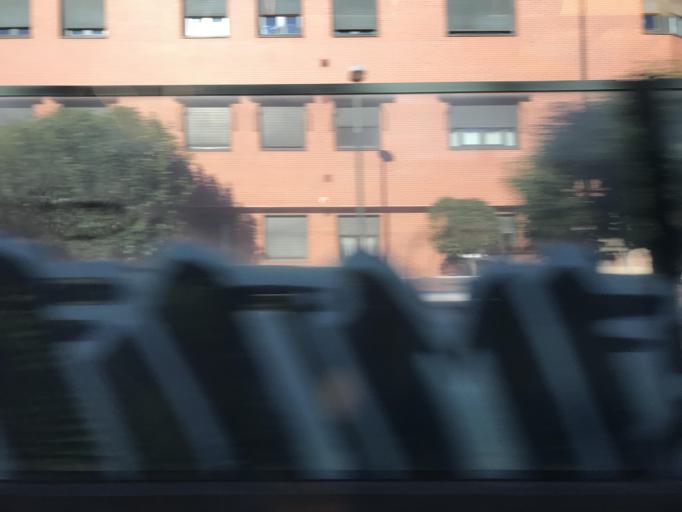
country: ES
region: Castille and Leon
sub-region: Provincia de Valladolid
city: Valladolid
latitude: 41.6326
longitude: -4.7360
